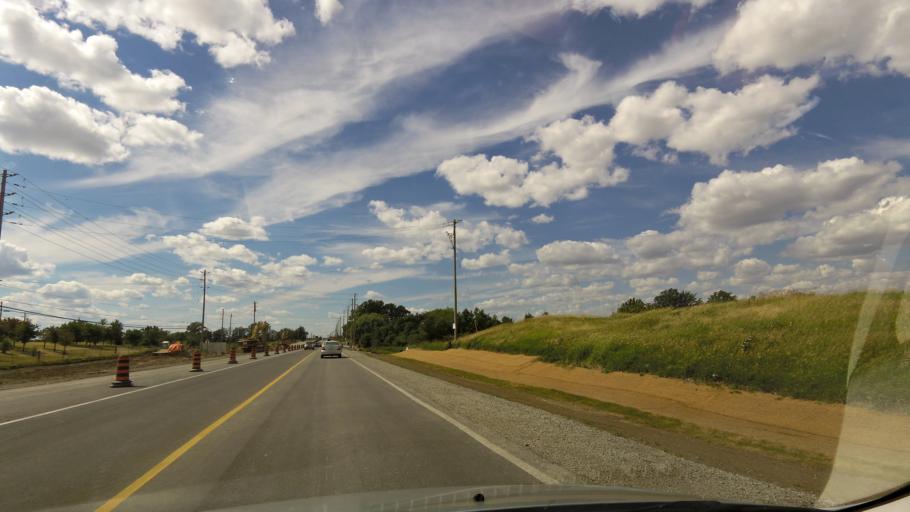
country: CA
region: Ontario
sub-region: Halton
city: Milton
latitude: 43.4778
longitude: -79.8222
